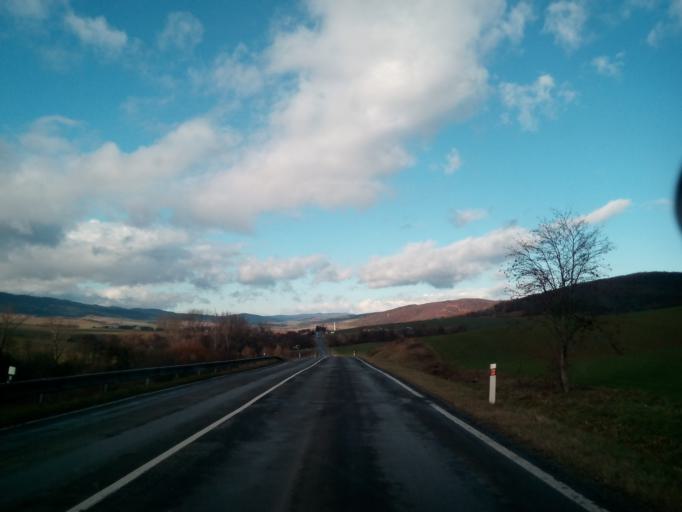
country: SK
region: Presovsky
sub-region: Okres Bardejov
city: Bardejov
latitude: 49.2370
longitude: 21.2774
